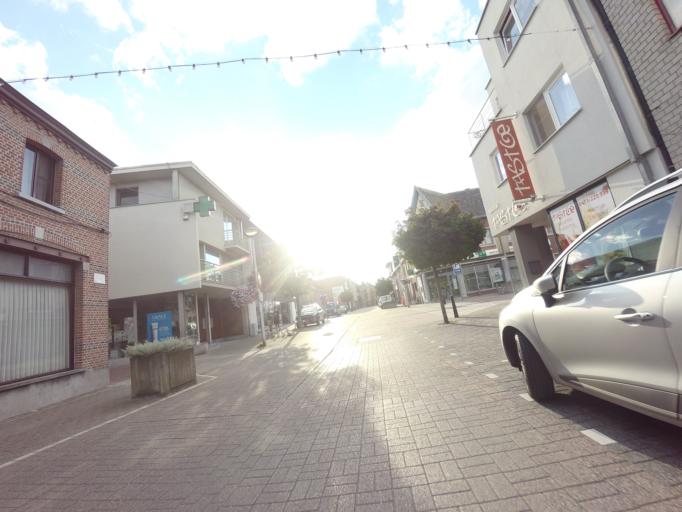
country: BE
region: Flanders
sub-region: Provincie Vlaams-Brabant
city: Kapelle-op-den-Bos
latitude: 51.0124
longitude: 4.3598
